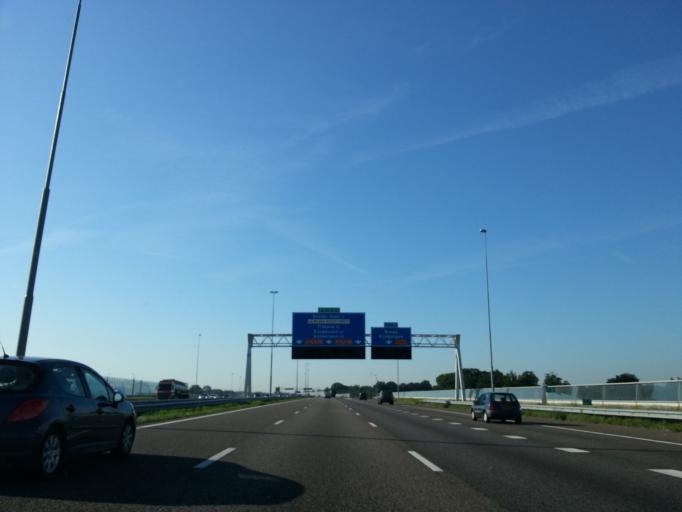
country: NL
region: North Brabant
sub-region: Gemeente Breda
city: Breda
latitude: 51.5685
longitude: 4.7301
